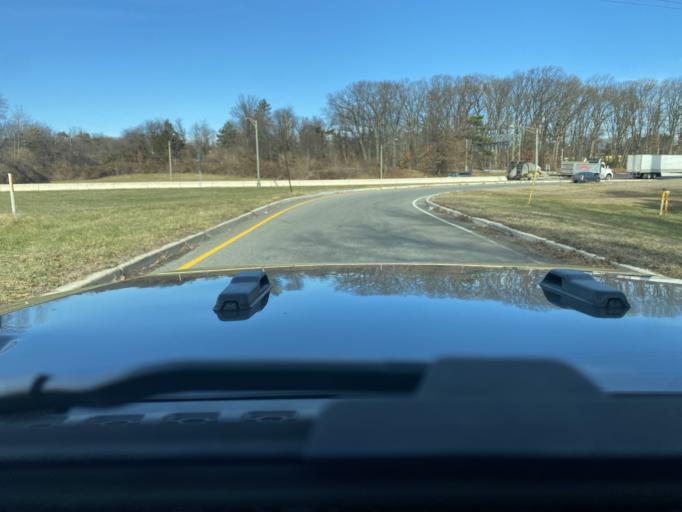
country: US
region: New Jersey
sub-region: Middlesex County
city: Metuchen
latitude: 40.5253
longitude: -74.3573
